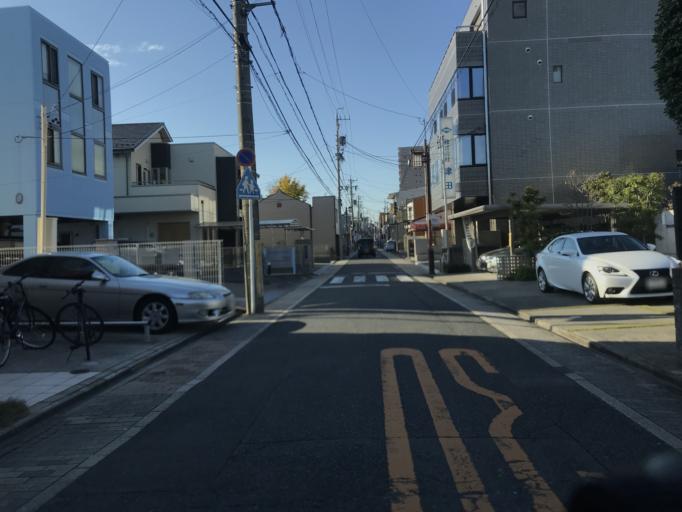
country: JP
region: Aichi
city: Nagoya-shi
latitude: 35.1885
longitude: 136.8797
